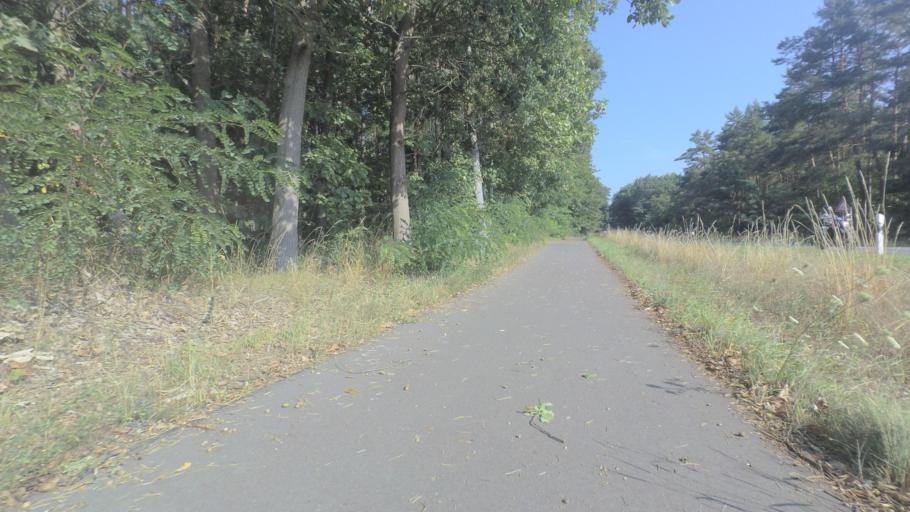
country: DE
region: Mecklenburg-Vorpommern
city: Malchow
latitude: 53.5005
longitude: 12.4220
